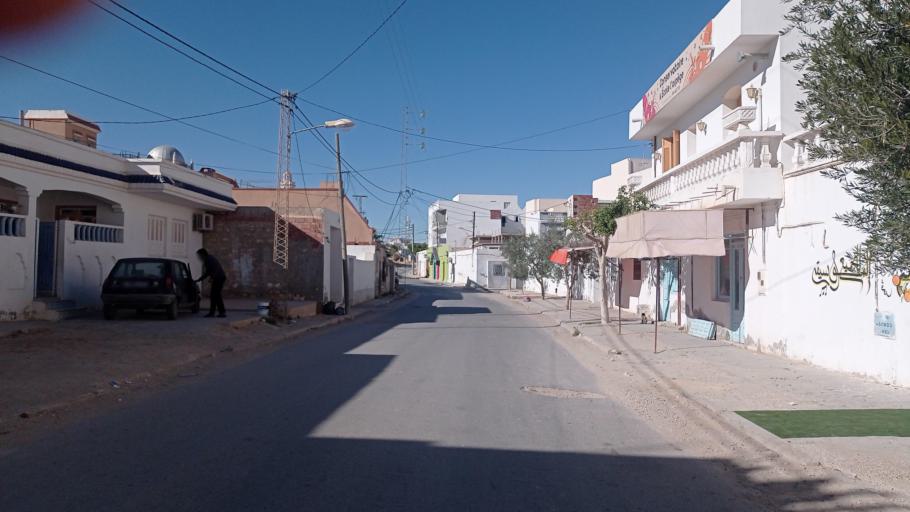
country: TN
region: Qabis
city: Gabes
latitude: 33.8475
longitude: 10.1096
